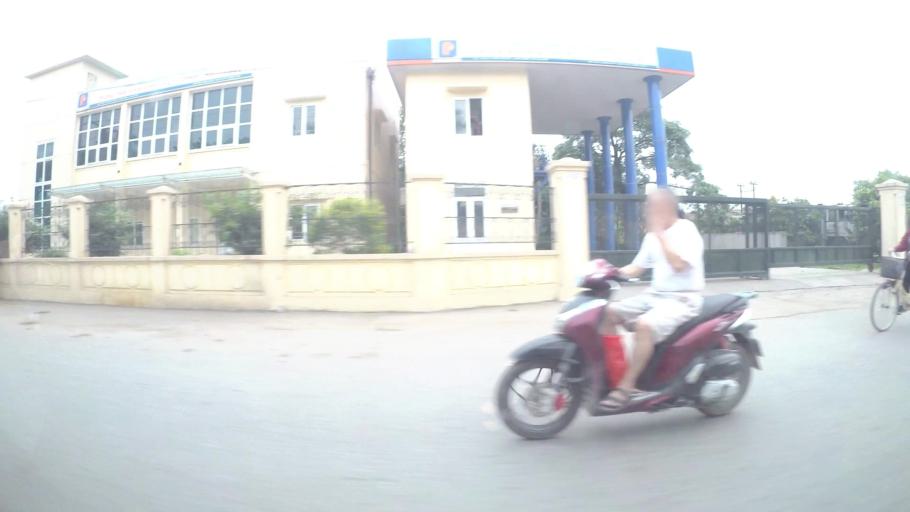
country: VN
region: Ha Noi
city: Hoan Kiem
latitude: 21.0656
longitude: 105.8930
